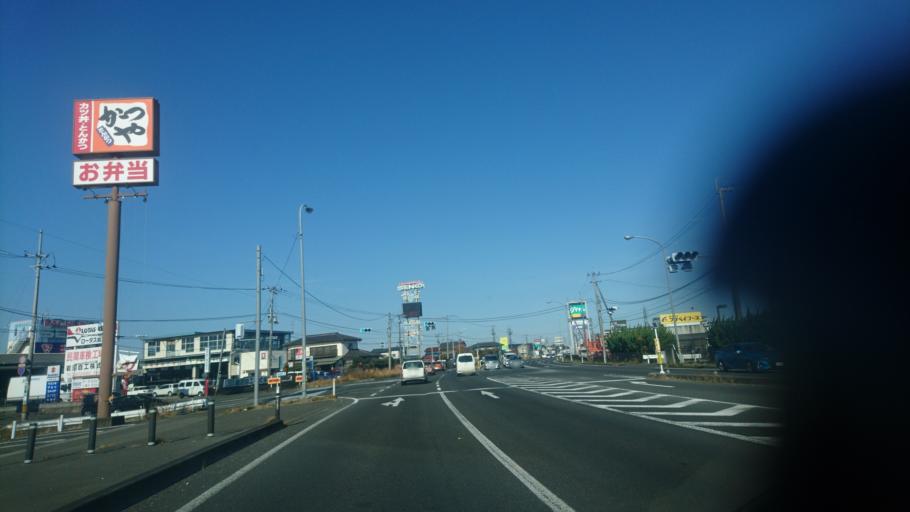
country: JP
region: Miyagi
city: Iwanuma
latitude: 38.1239
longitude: 140.8730
